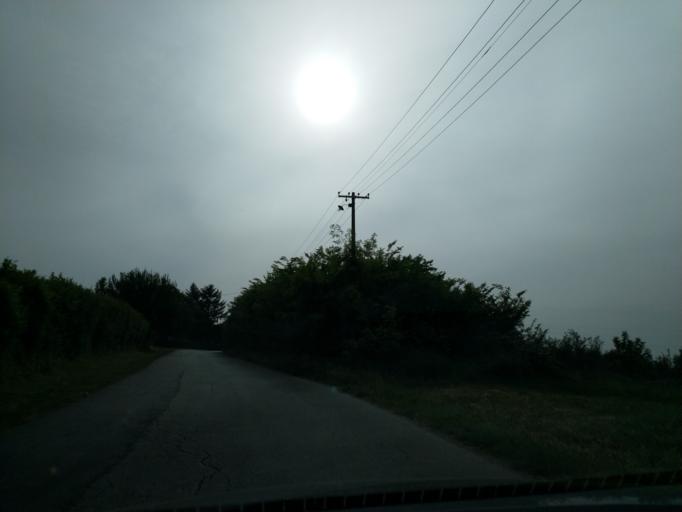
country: RS
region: Central Serbia
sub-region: Pomoravski Okrug
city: Jagodina
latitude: 43.9741
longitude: 21.2078
